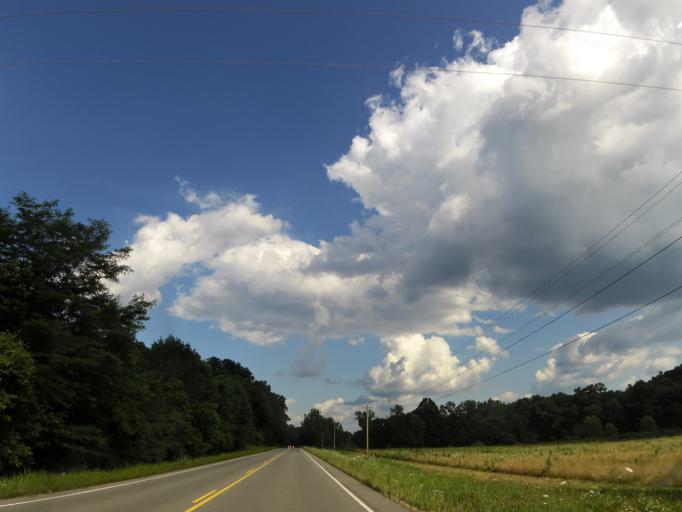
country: US
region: Tennessee
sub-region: Perry County
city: Linden
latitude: 35.6112
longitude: -87.7196
